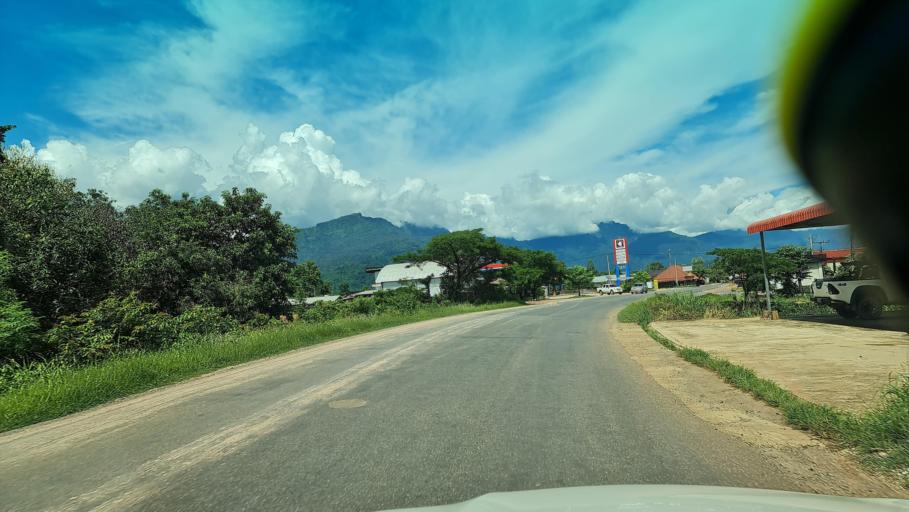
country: LA
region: Bolikhamxai
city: Ban Nahin
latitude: 18.3011
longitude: 104.1109
